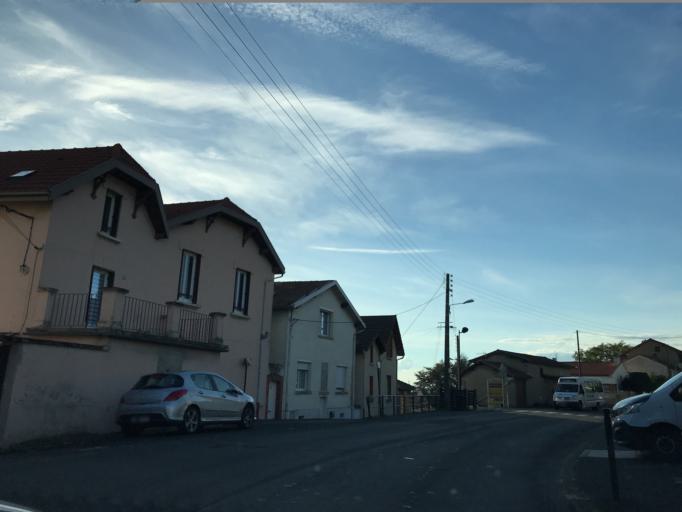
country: FR
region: Auvergne
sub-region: Departement du Puy-de-Dome
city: Thiers
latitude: 45.8603
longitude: 3.5375
